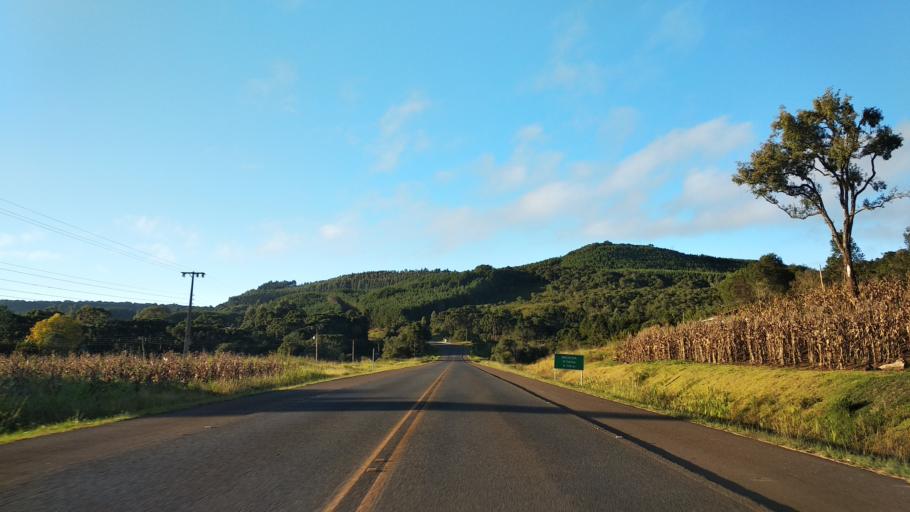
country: BR
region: Santa Catarina
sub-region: Curitibanos
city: Curitibanos
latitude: -27.5977
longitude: -50.7305
